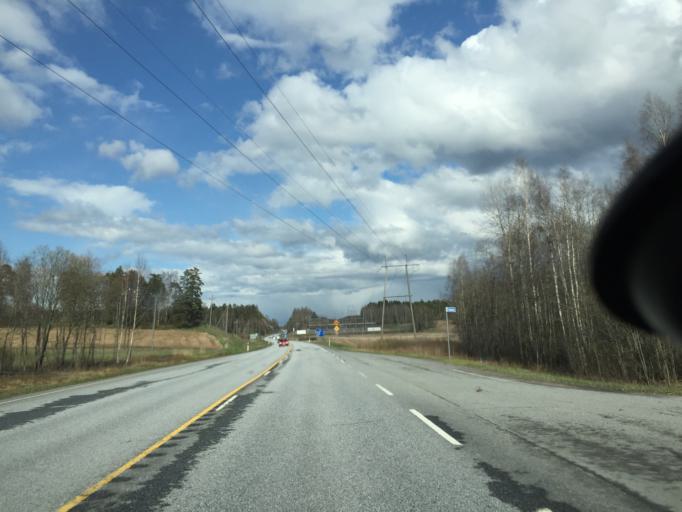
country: FI
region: Uusimaa
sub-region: Raaseporin
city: Karis
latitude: 60.0446
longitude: 23.6292
